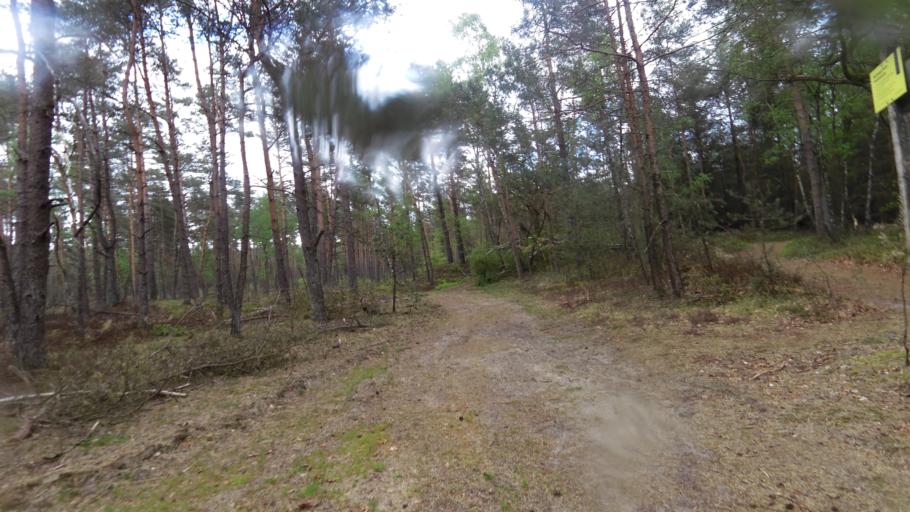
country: NL
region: Gelderland
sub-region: Gemeente Apeldoorn
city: Loenen
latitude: 52.0742
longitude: 6.0084
